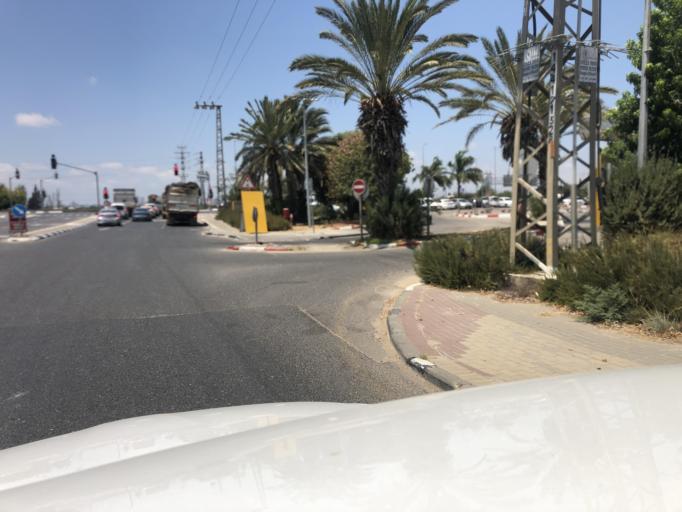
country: IL
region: Central District
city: Jaljulya
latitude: 32.1453
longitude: 34.9473
